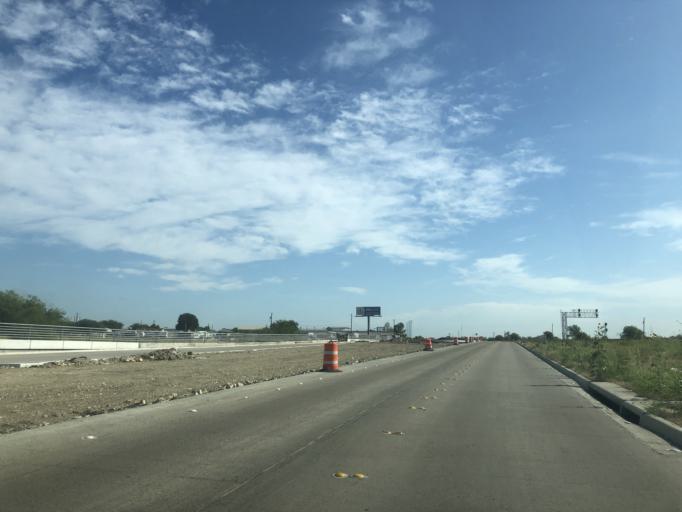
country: US
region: Texas
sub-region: Denton County
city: Justin
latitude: 33.0550
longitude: -97.3010
